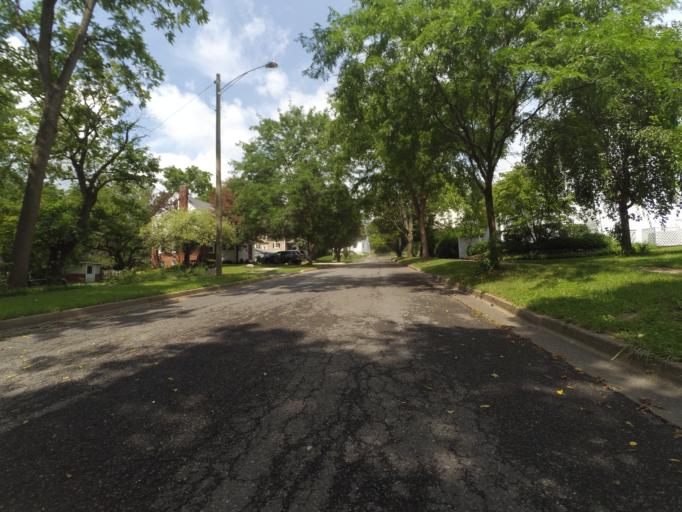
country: US
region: Pennsylvania
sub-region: Centre County
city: State College
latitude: 40.7894
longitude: -77.8551
